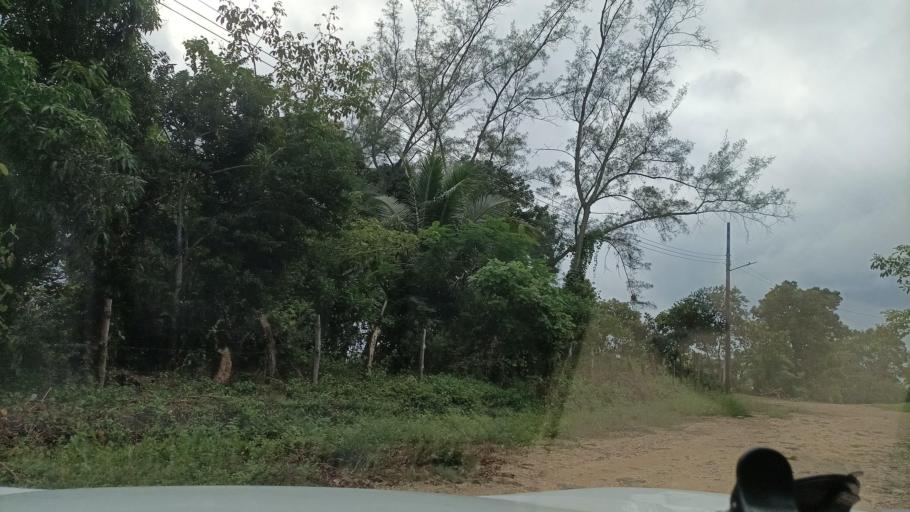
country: MX
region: Veracruz
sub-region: Moloacan
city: Cuichapa
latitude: 17.9214
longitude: -94.3663
